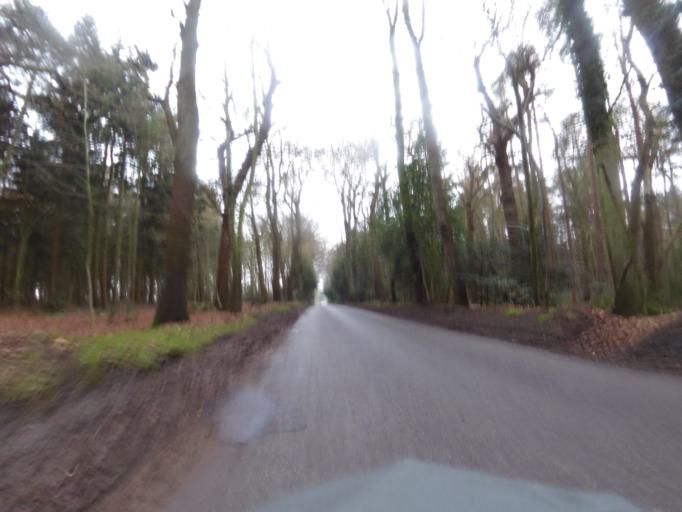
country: GB
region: England
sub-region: Norfolk
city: Briston
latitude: 52.8616
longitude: 1.0664
